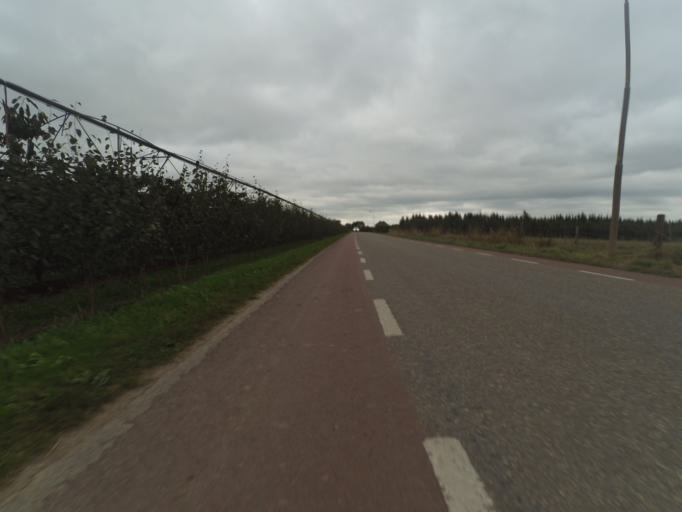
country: NL
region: Utrecht
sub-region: Gemeente Rhenen
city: Rhenen
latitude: 51.9451
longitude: 5.5460
